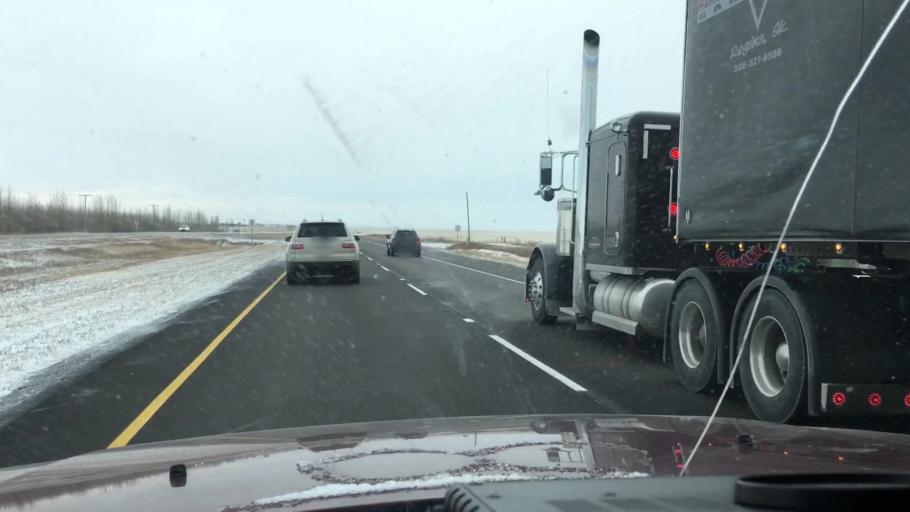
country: CA
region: Saskatchewan
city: Saskatoon
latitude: 51.7711
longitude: -106.4763
